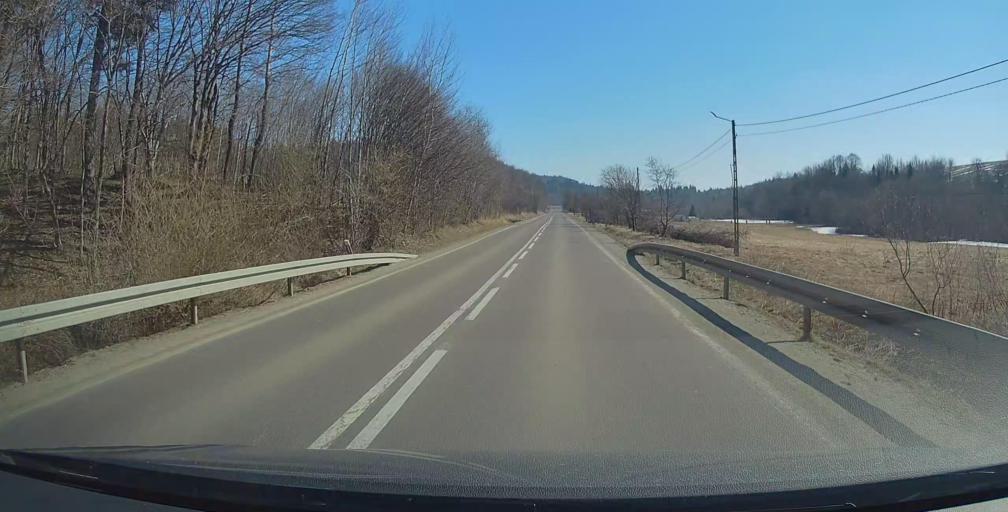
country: PL
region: Subcarpathian Voivodeship
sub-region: Powiat bieszczadzki
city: Ustrzyki Dolne
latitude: 49.5351
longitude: 22.5972
